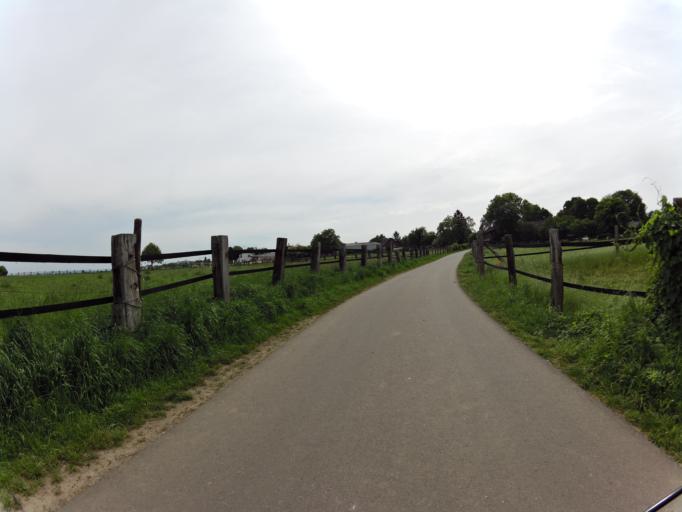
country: DE
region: North Rhine-Westphalia
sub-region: Regierungsbezirk Koln
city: Wurselen
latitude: 50.8295
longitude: 6.1405
